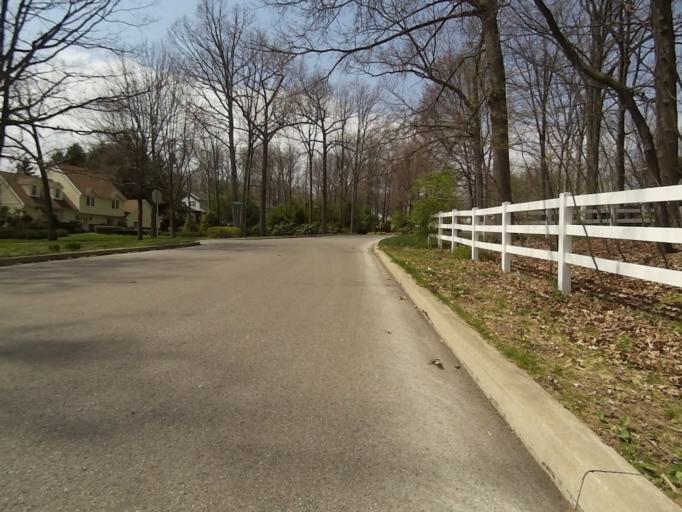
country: US
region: Pennsylvania
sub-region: Centre County
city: Park Forest Village
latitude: 40.7963
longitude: -77.9040
